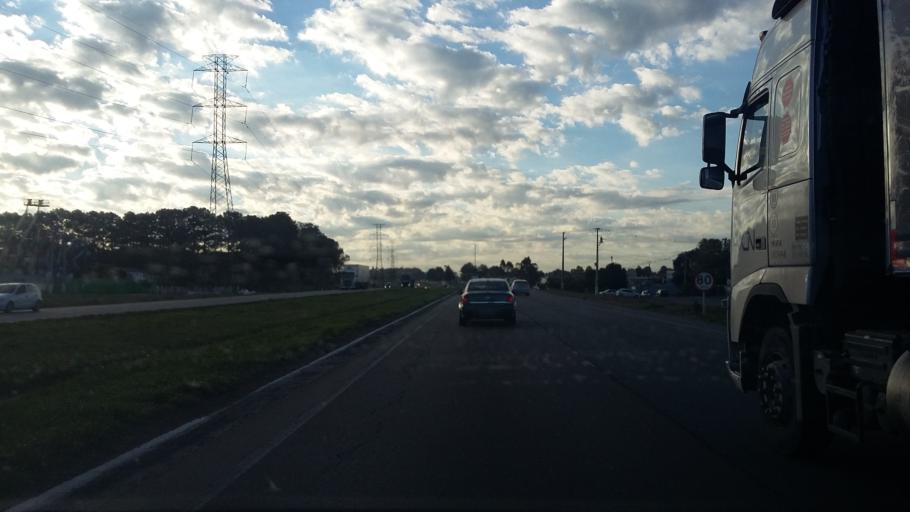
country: BR
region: Parana
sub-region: Curitiba
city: Curitiba
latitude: -25.4780
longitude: -49.3503
